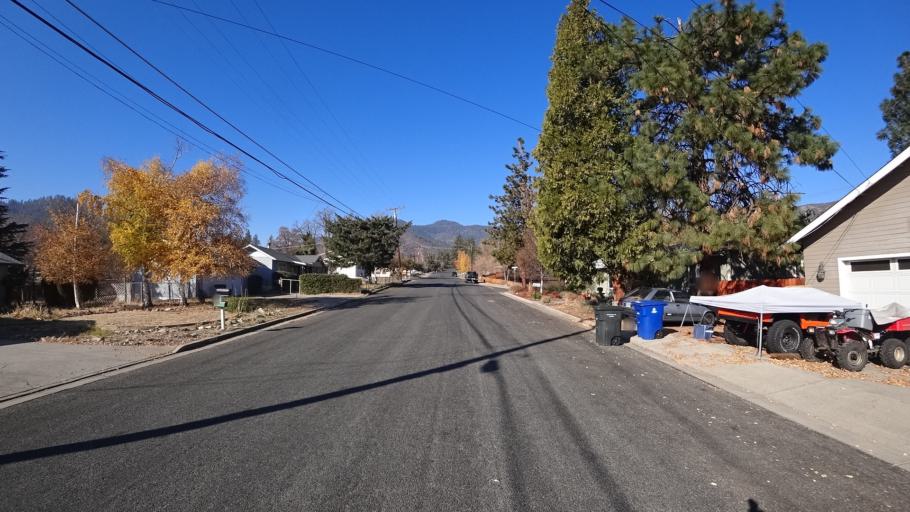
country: US
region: California
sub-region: Siskiyou County
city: Yreka
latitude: 41.7356
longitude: -122.6497
